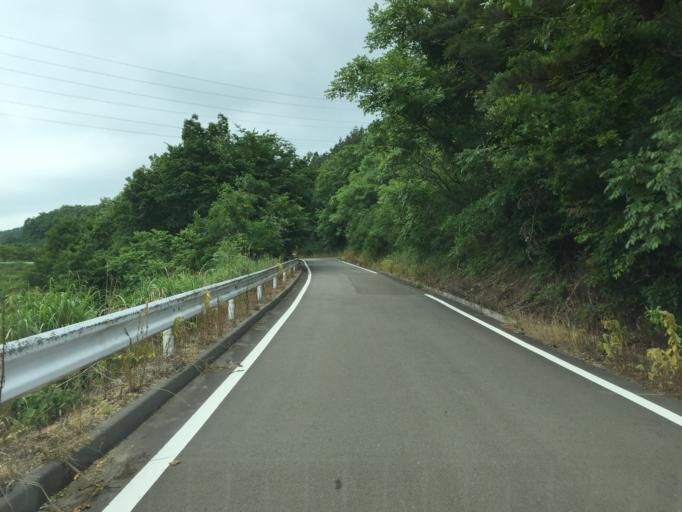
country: JP
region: Miyagi
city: Marumori
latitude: 37.8013
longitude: 140.7626
